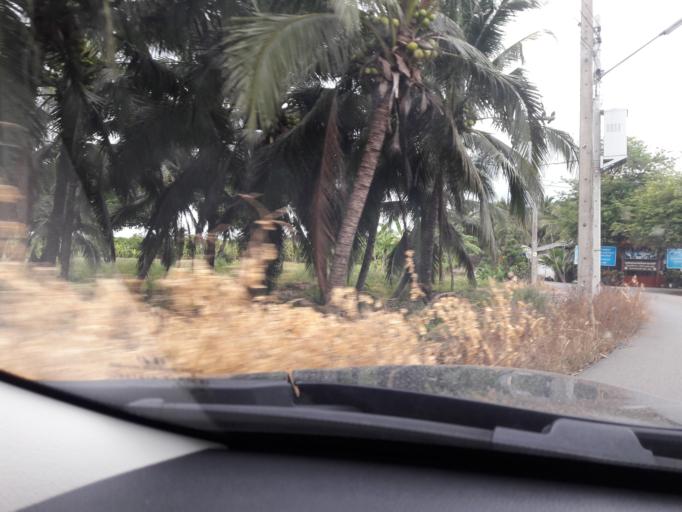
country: TH
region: Ratchaburi
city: Bang Phae
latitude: 13.6268
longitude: 99.9550
